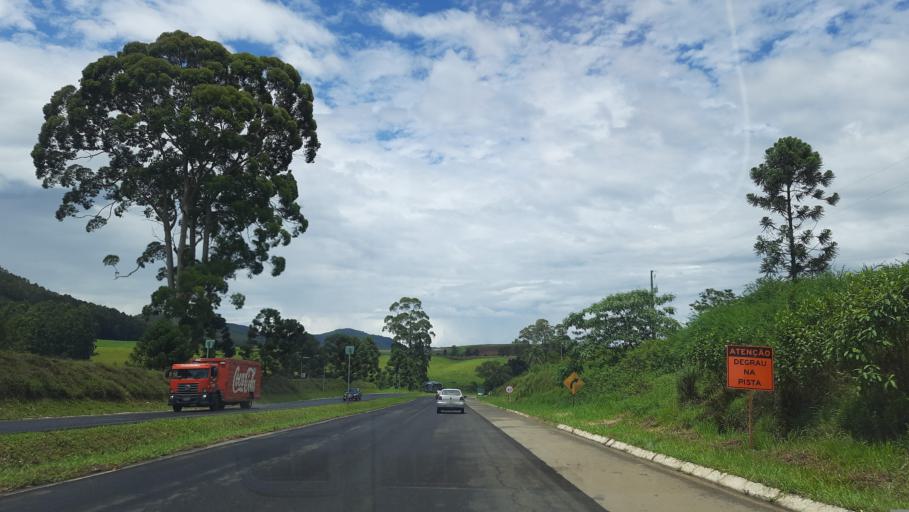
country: BR
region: Minas Gerais
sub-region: Pocos De Caldas
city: Pocos de Caldas
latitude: -21.8392
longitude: -46.6756
